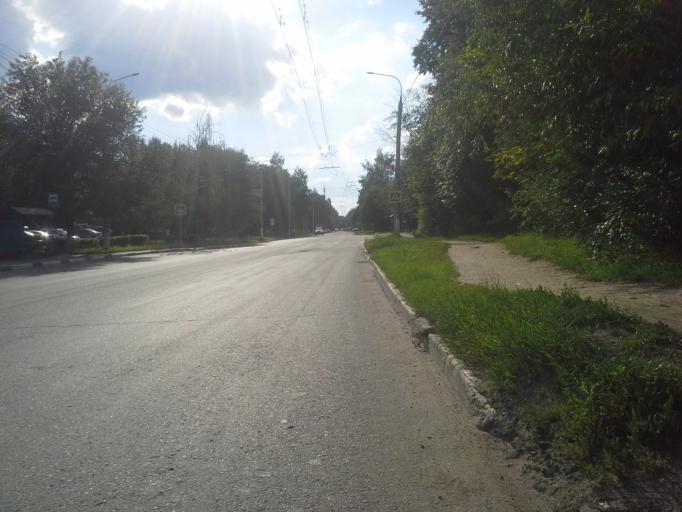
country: RU
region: Moskovskaya
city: Dubrovitsy
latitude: 55.4345
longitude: 37.5070
